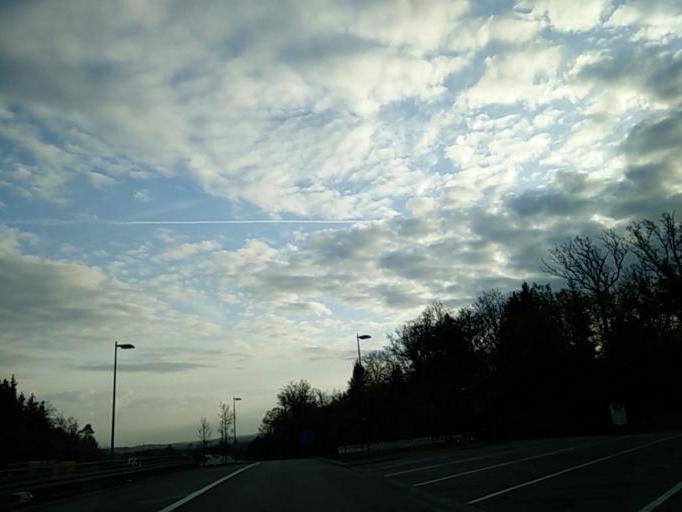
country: DE
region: Baden-Wuerttemberg
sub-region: Regierungsbezirk Stuttgart
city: Nufringen
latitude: 48.6168
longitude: 8.9077
